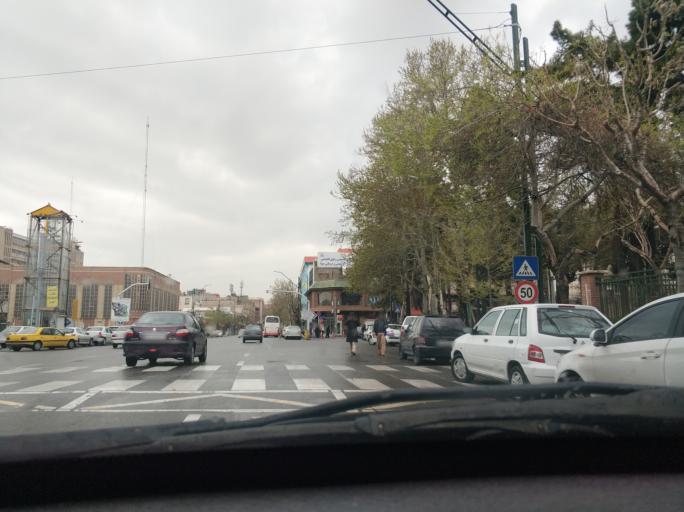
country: IR
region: Tehran
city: Tehran
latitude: 35.6859
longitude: 51.4151
